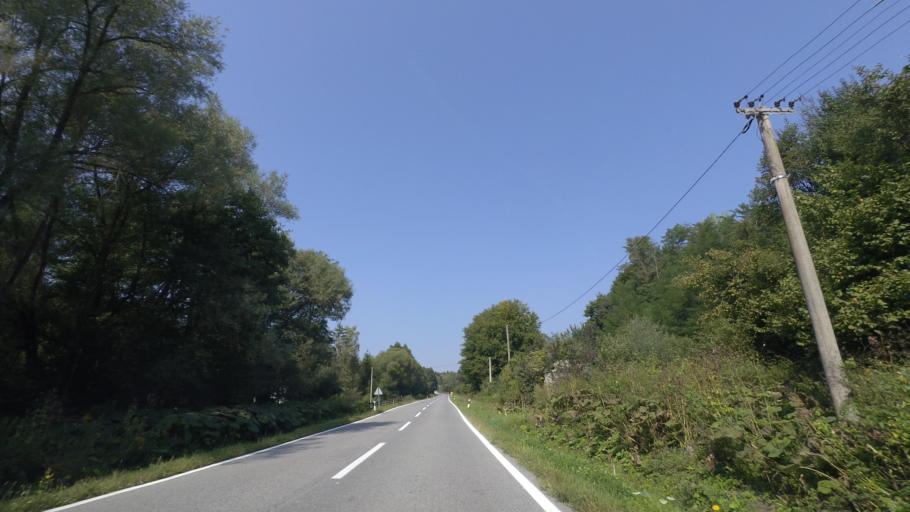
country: HR
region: Bjelovarsko-Bilogorska
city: Sirac
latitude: 45.4609
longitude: 17.4148
